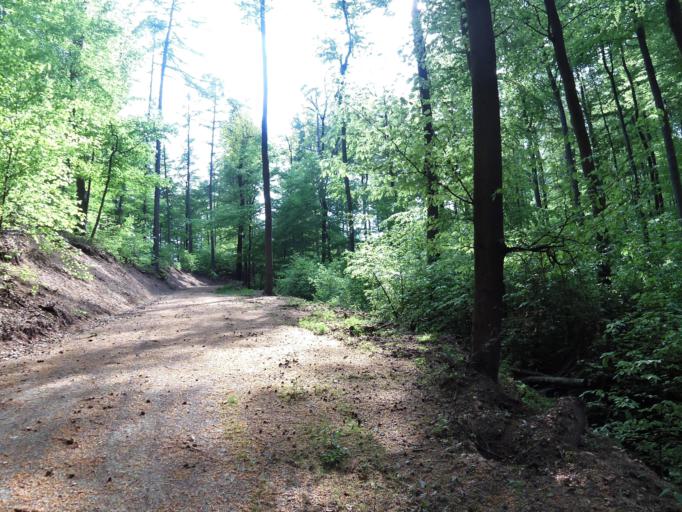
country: DE
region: Thuringia
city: Wolfsburg-Unkeroda
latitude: 50.9482
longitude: 10.2808
